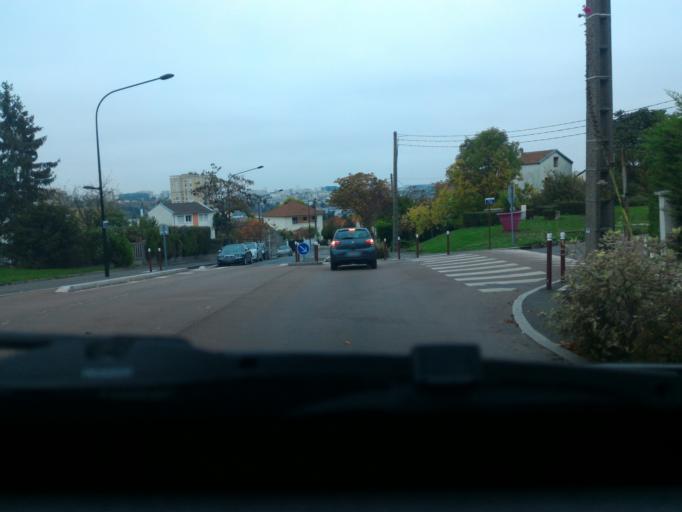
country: FR
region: Ile-de-France
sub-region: Departement du Val-de-Marne
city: L'Hay-les-Roses
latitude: 48.7855
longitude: 2.3380
